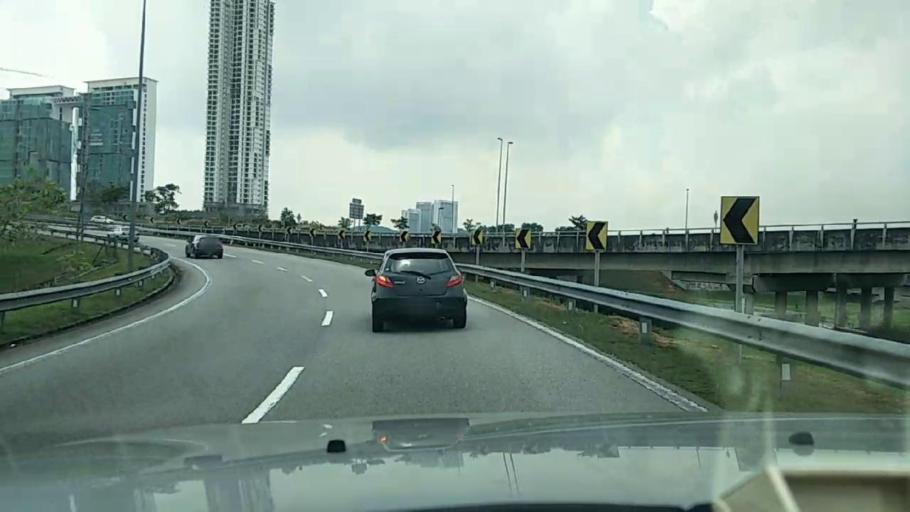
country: MY
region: Putrajaya
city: Putrajaya
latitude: 2.9445
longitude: 101.6506
